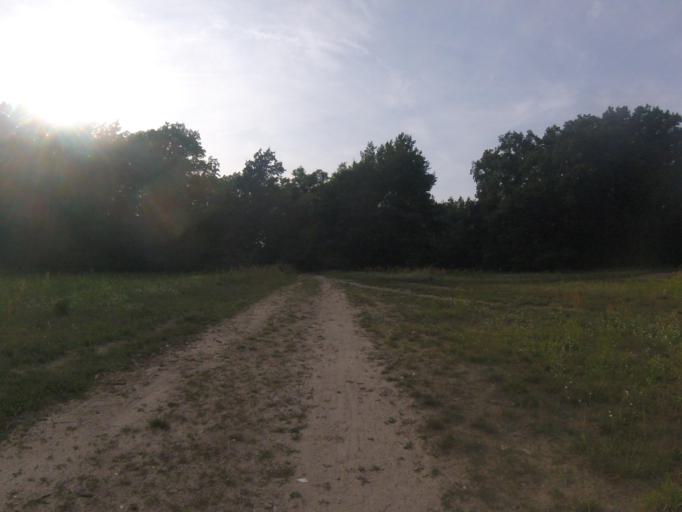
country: DE
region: Berlin
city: Lichtenrade
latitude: 52.3556
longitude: 13.4557
